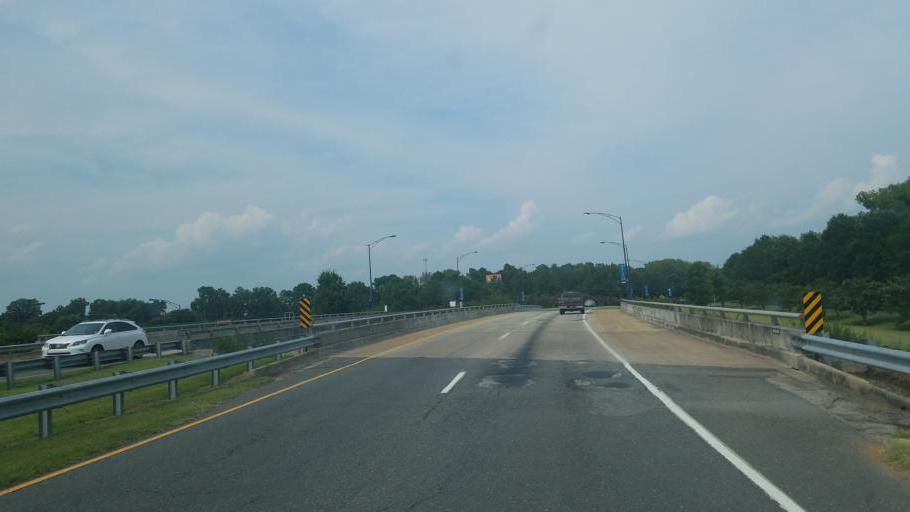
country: US
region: South Carolina
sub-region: York County
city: Rock Hill
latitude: 34.9384
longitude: -80.9980
